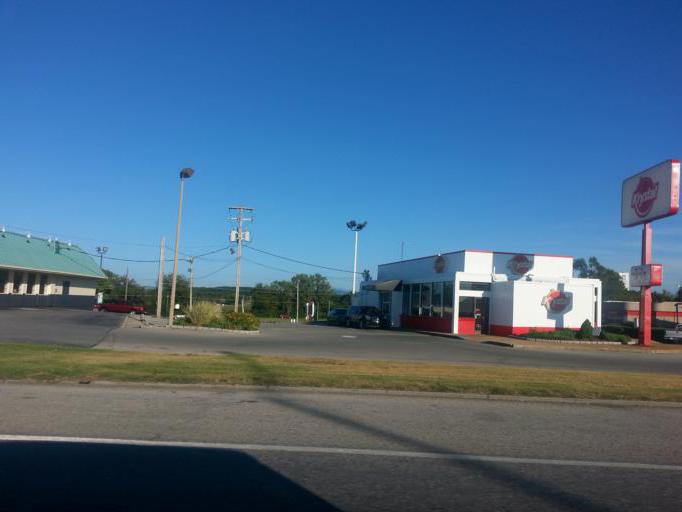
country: US
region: Tennessee
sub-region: Blount County
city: Alcoa
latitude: 35.8186
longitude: -83.9799
